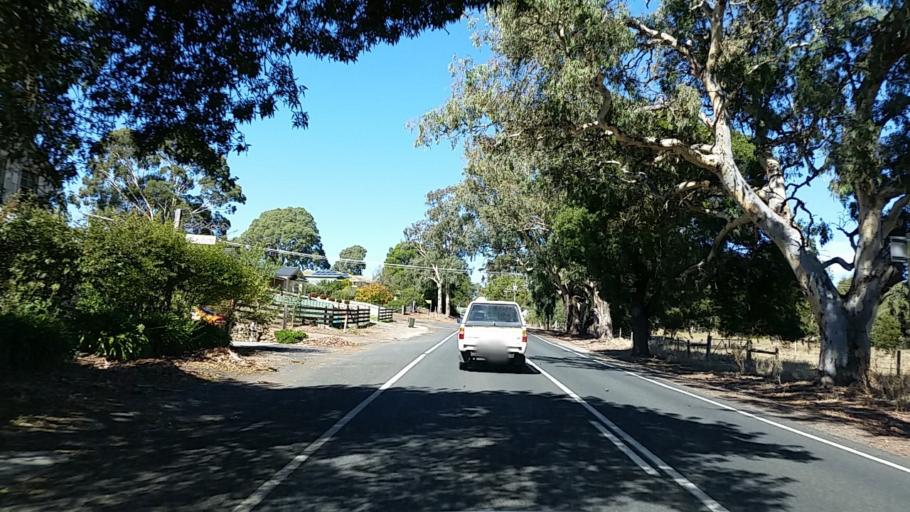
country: AU
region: South Australia
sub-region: Adelaide Hills
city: Birdwood
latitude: -34.7791
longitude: 139.0351
